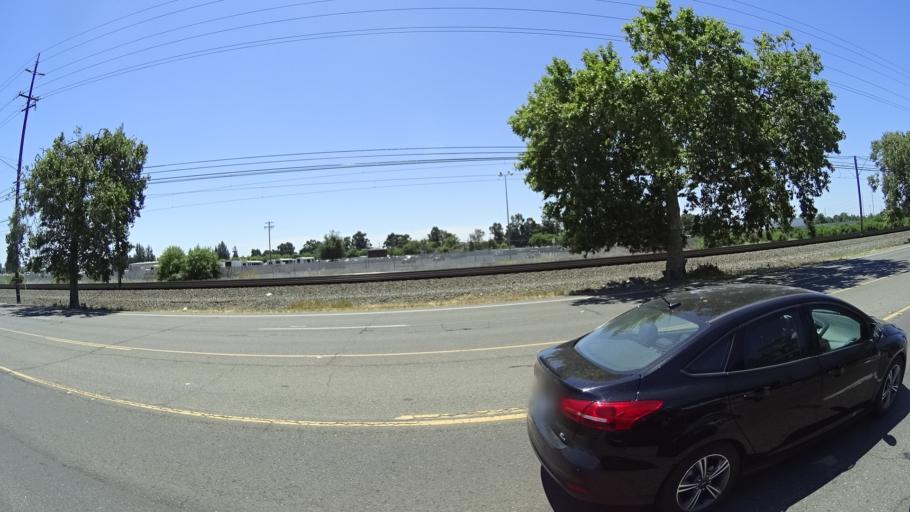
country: US
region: California
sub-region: Sacramento County
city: Rosemont
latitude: 38.5497
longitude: -121.3831
